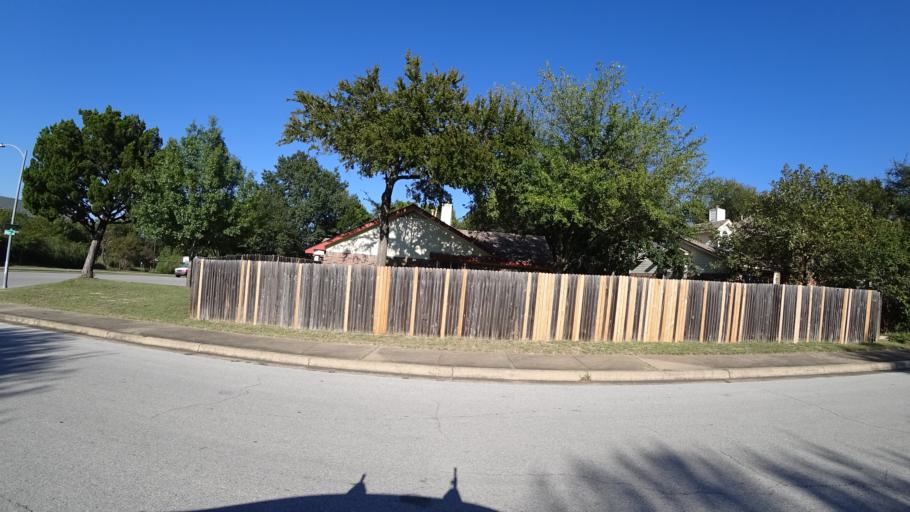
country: US
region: Texas
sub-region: Travis County
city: Austin
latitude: 30.2210
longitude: -97.7246
